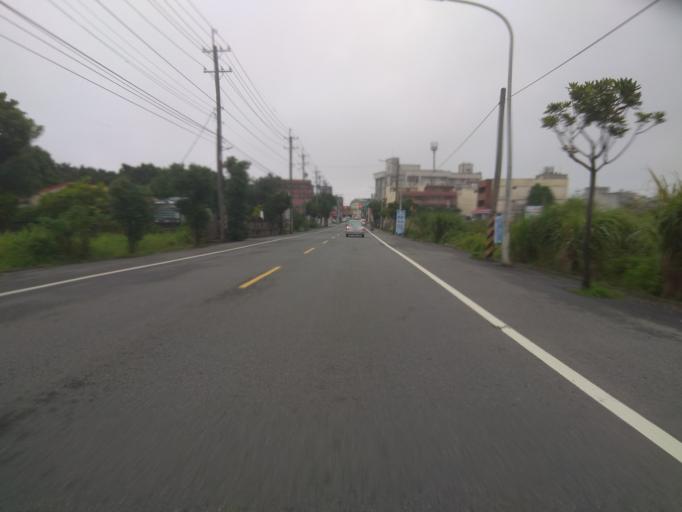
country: TW
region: Taiwan
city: Taoyuan City
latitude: 25.0099
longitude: 121.1354
